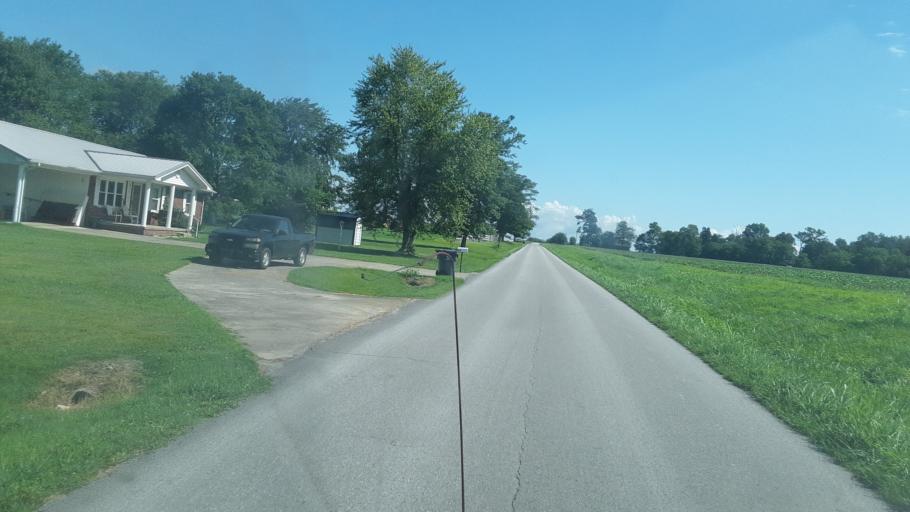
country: US
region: Kentucky
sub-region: Todd County
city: Elkton
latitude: 36.8049
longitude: -87.1852
